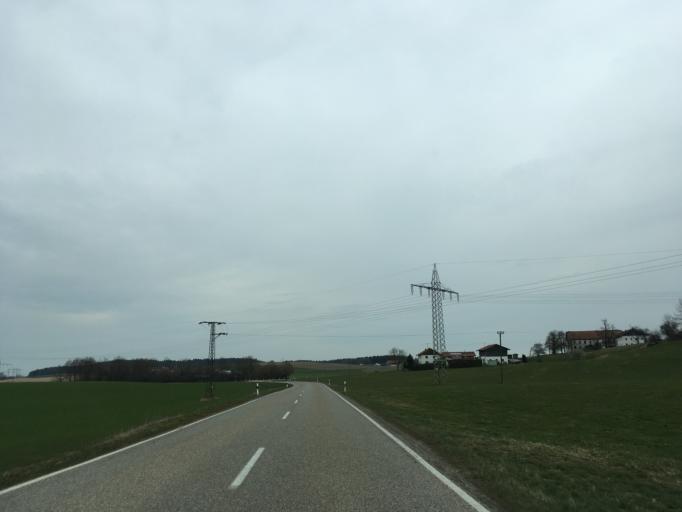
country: DE
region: Bavaria
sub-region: Upper Bavaria
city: Schnaitsee
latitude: 48.0431
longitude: 12.3712
